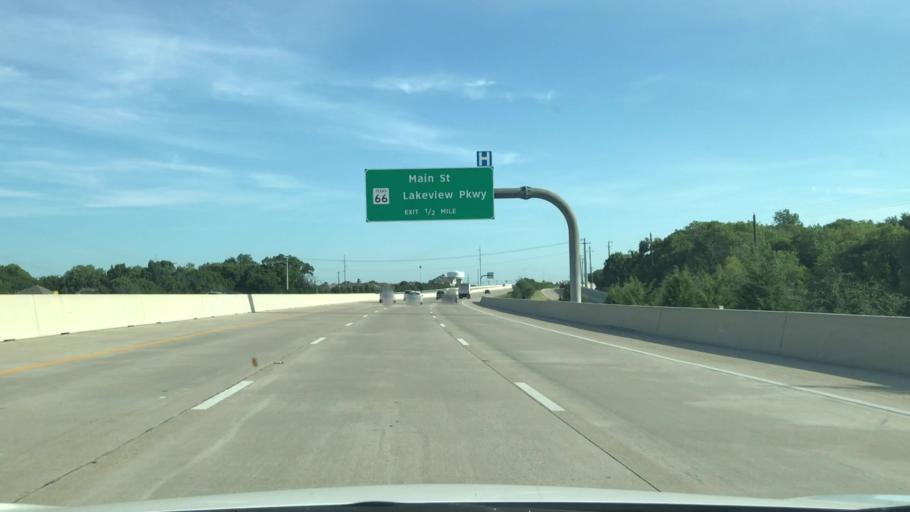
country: US
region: Texas
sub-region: Dallas County
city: Rowlett
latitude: 32.8842
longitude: -96.5561
